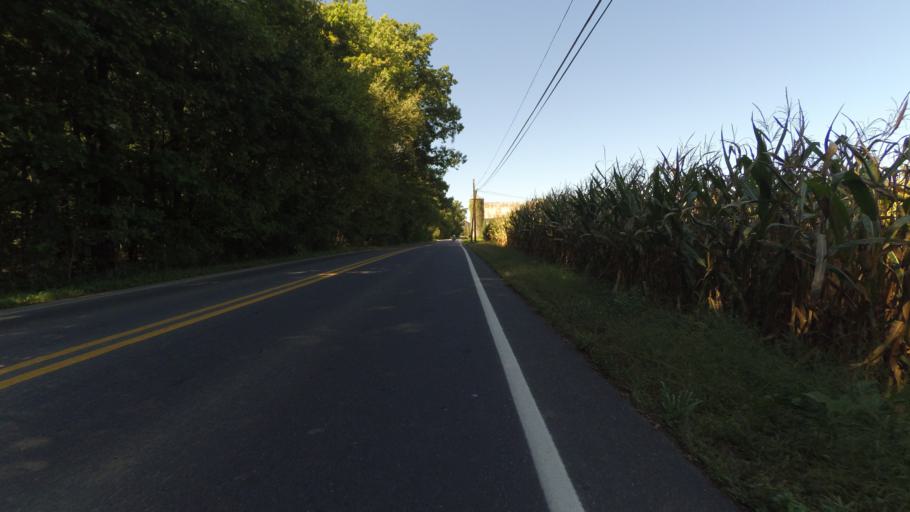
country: US
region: Pennsylvania
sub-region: Centre County
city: Pine Grove Mills
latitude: 40.7626
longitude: -77.9123
